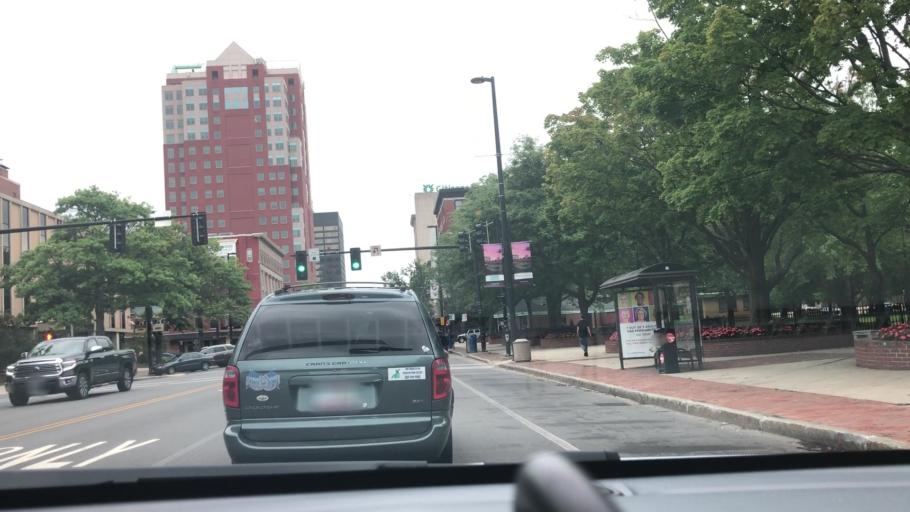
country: US
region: New Hampshire
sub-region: Hillsborough County
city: Manchester
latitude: 42.9883
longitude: -71.4630
